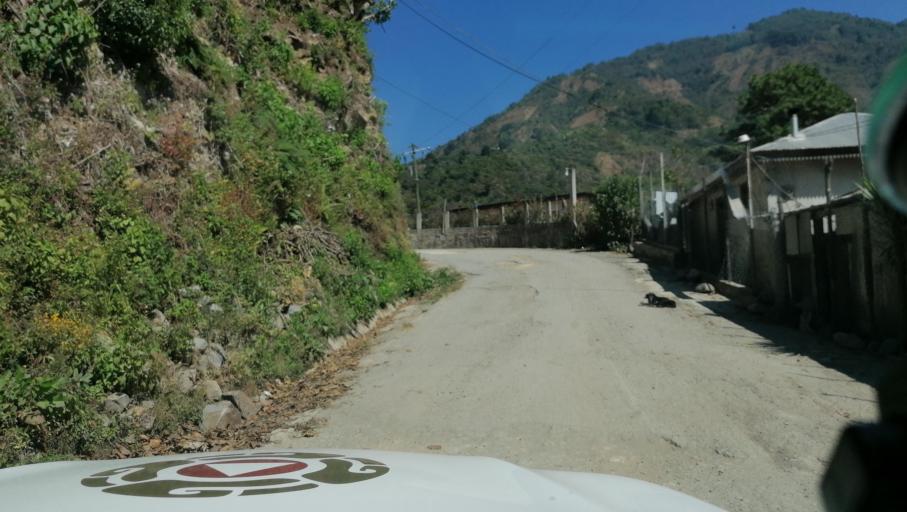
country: GT
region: San Marcos
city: Tacana
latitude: 15.1929
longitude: -92.1860
